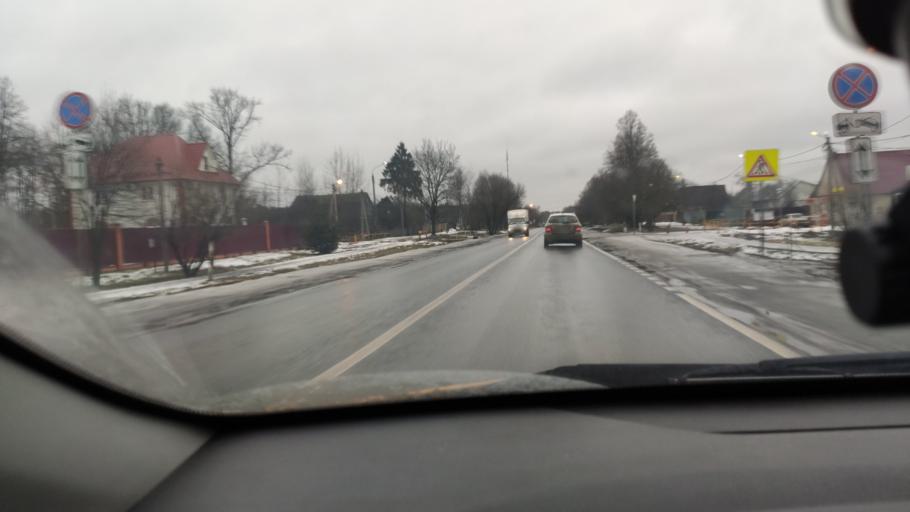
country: RU
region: Moskovskaya
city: Troitsk
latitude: 55.2951
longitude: 37.1901
